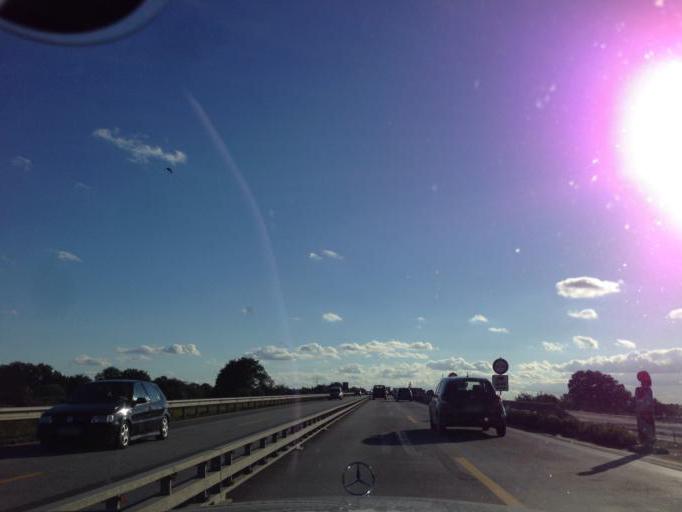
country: DE
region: Schleswig-Holstein
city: Krogaspe
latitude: 54.1171
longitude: 9.9495
